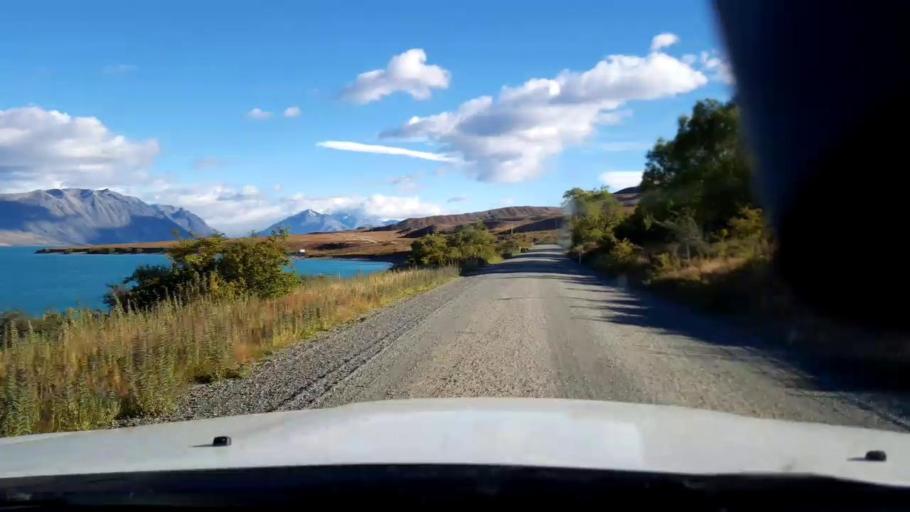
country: NZ
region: Canterbury
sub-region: Timaru District
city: Pleasant Point
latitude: -43.9313
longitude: 170.5593
